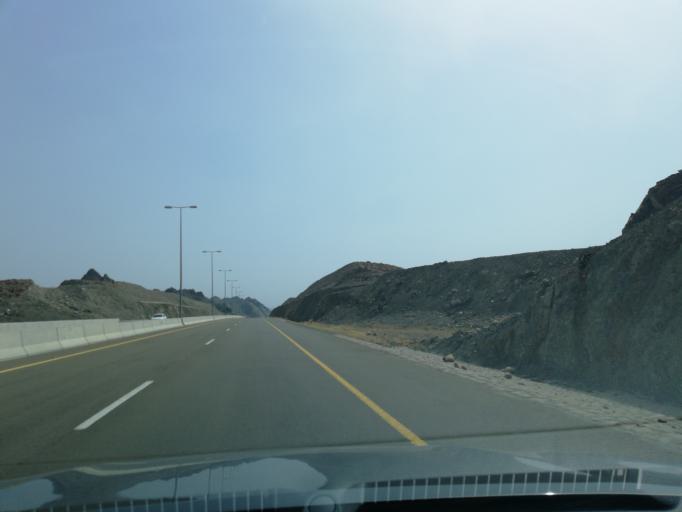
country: OM
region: Al Batinah
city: Al Liwa'
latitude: 24.2750
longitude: 56.3963
